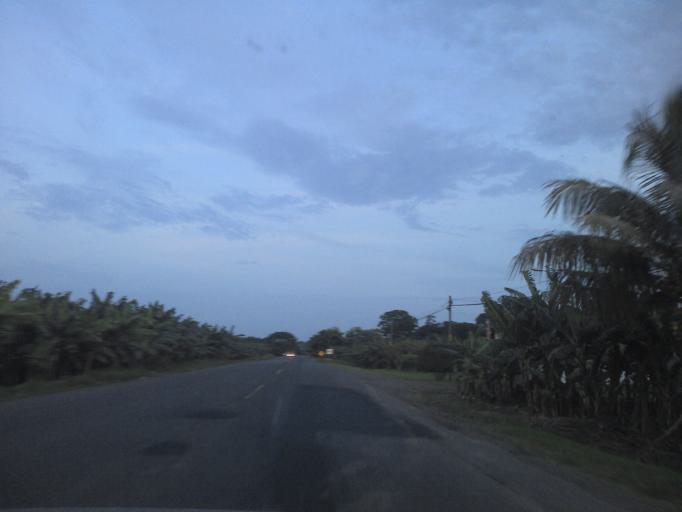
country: MX
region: Veracruz
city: San Rafael
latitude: 20.1851
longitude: -96.8398
